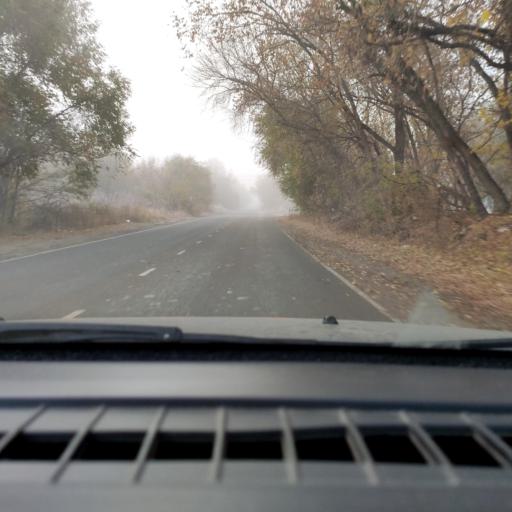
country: RU
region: Samara
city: Tol'yatti
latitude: 53.5840
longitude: 49.2569
